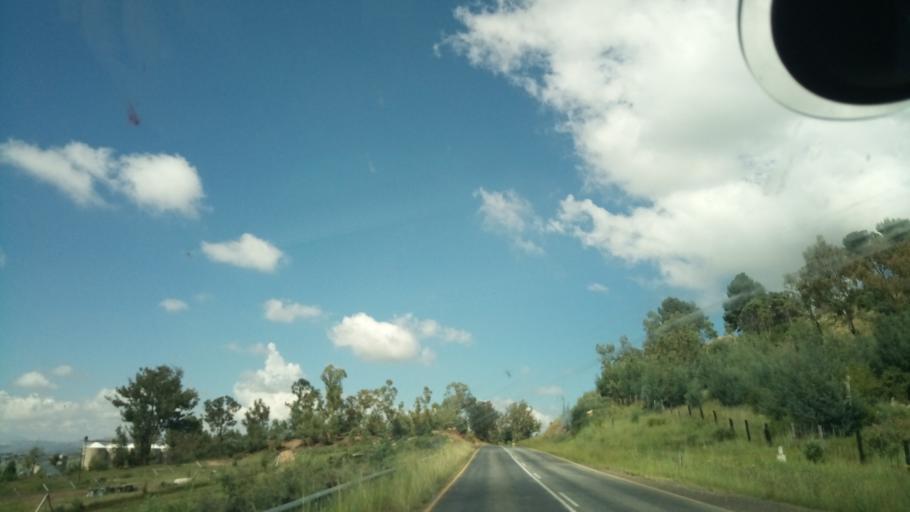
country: ZA
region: Orange Free State
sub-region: Thabo Mofutsanyana District Municipality
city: Ficksburg
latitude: -28.8610
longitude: 27.8752
